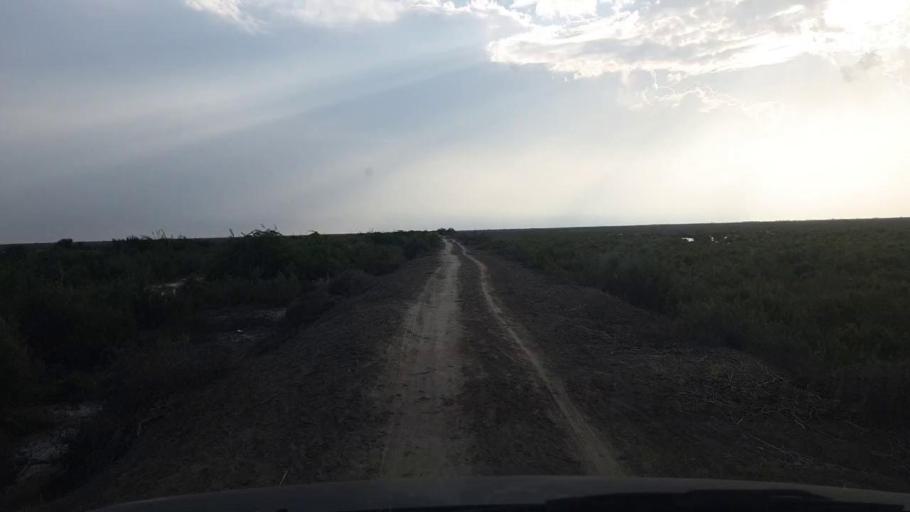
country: PK
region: Sindh
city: Badin
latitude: 24.4422
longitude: 68.6768
